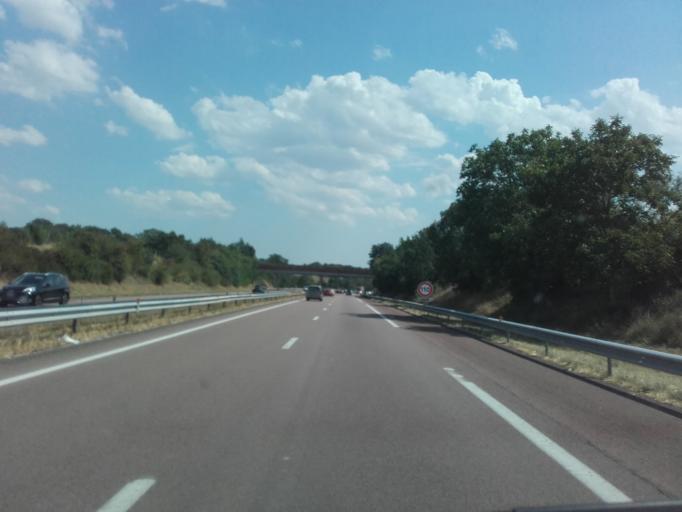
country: FR
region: Bourgogne
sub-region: Departement de l'Yonne
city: Avallon
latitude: 47.5605
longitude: 3.9455
